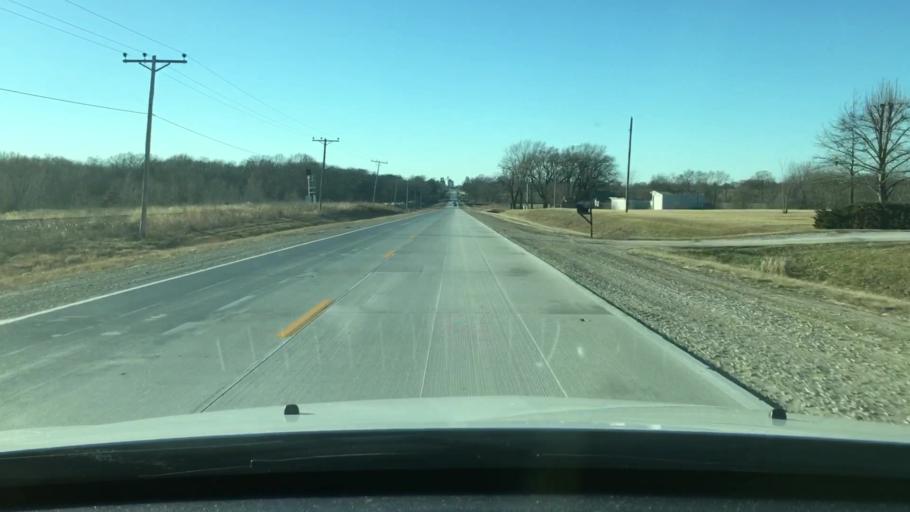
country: US
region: Missouri
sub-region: Boone County
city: Centralia
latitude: 39.2066
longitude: -92.0963
